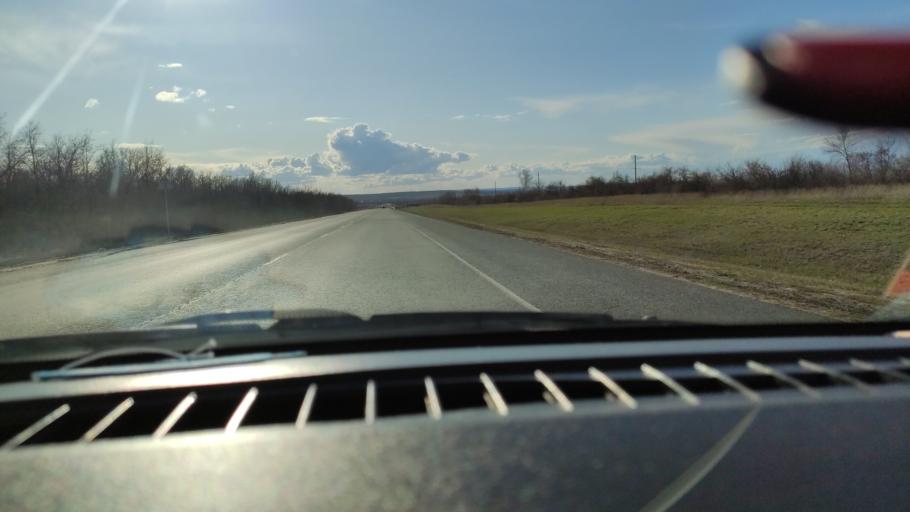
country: RU
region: Saratov
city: Yelshanka
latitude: 51.8273
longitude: 46.2709
